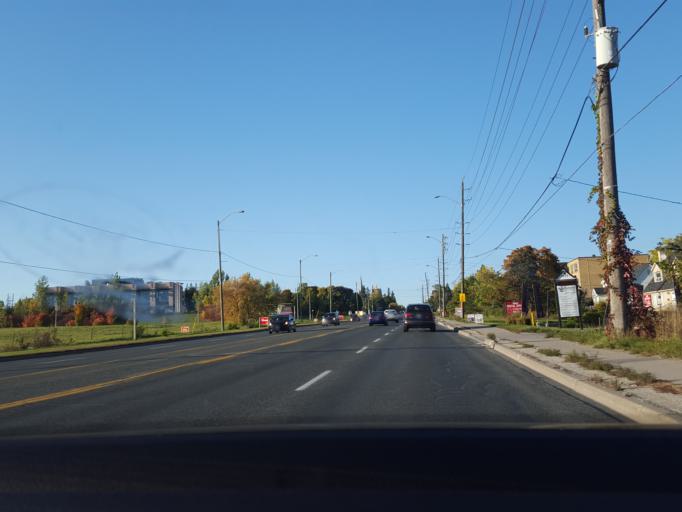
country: CA
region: Ontario
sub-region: York
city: Richmond Hill
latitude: 43.8677
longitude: -79.4363
